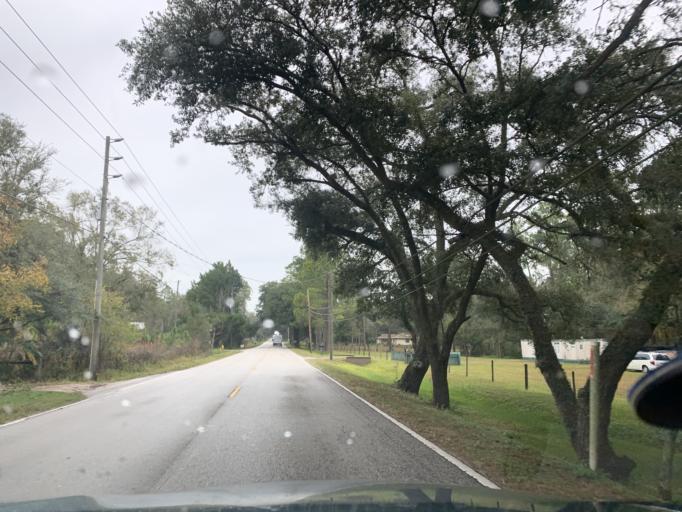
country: US
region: Florida
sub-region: Pasco County
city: Wesley Chapel
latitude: 28.2478
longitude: -82.3202
